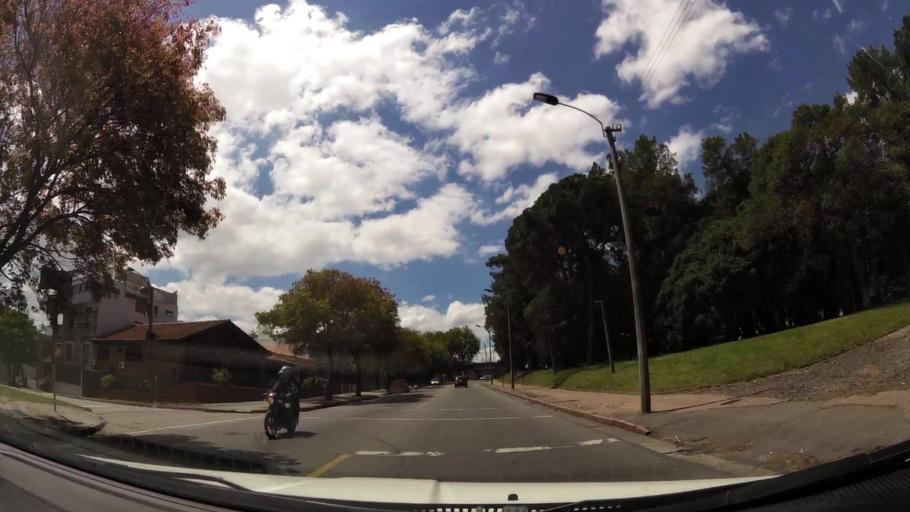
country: UY
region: Montevideo
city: Montevideo
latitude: -34.8567
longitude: -56.2121
